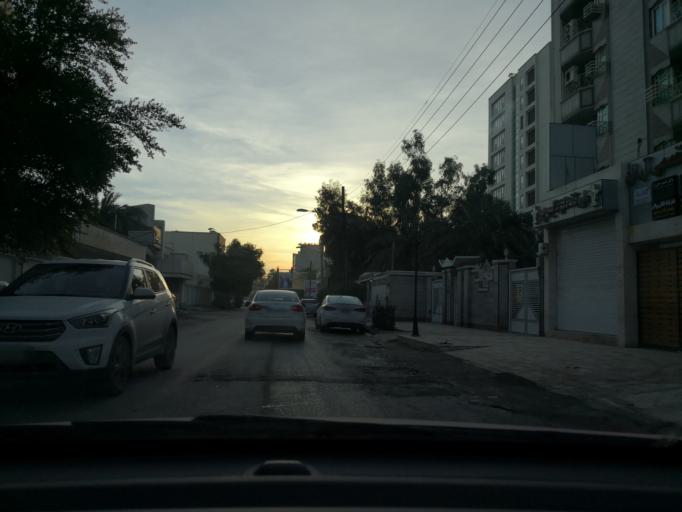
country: IR
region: Khuzestan
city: Ahvaz
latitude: 31.3505
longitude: 48.6858
